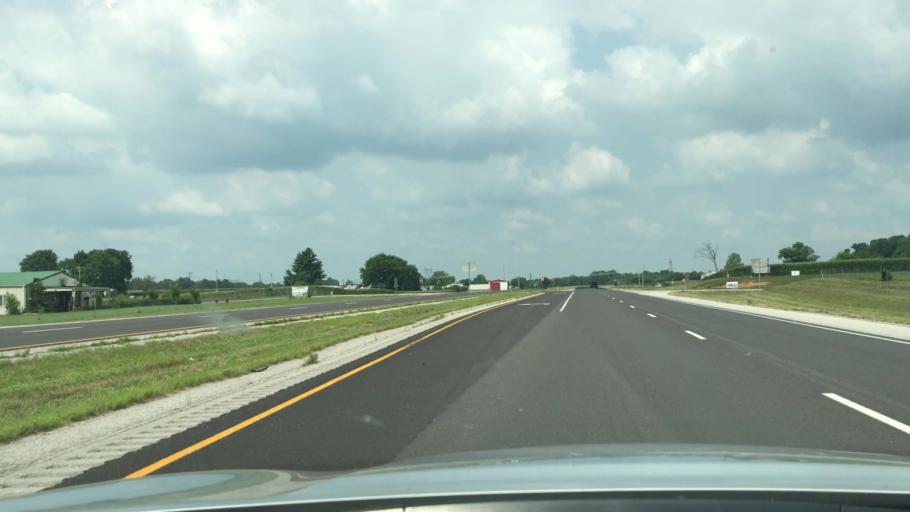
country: US
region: Kentucky
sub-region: Todd County
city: Elkton
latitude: 36.8029
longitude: -87.0932
